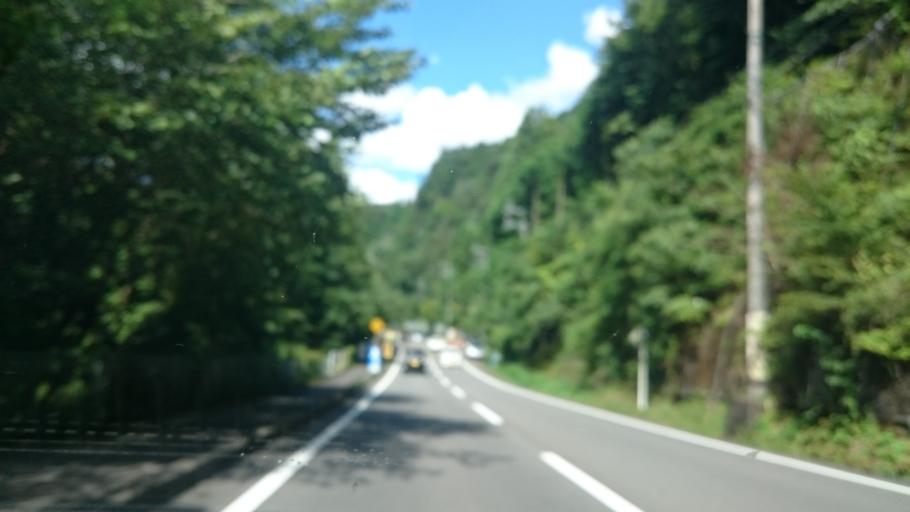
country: JP
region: Gifu
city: Nakatsugawa
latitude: 35.5972
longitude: 137.4625
